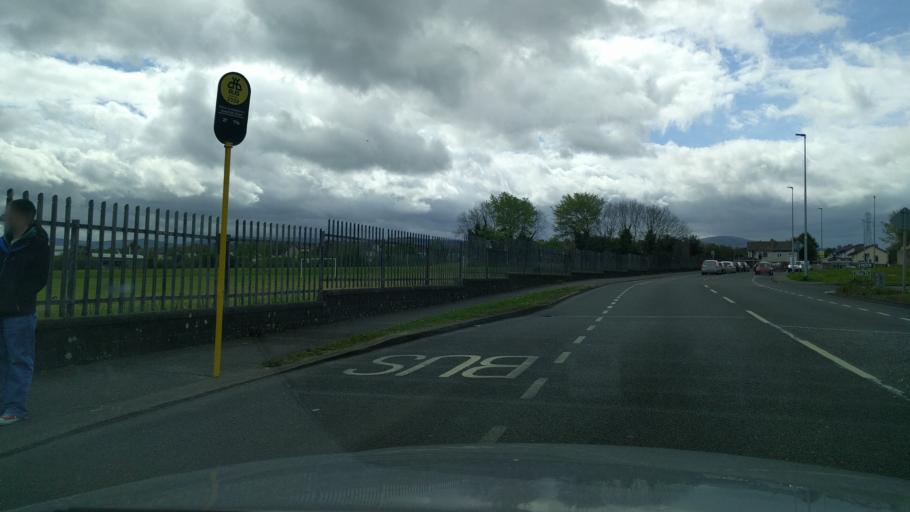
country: IE
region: Leinster
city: Firhouse
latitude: 53.3027
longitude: -6.3515
